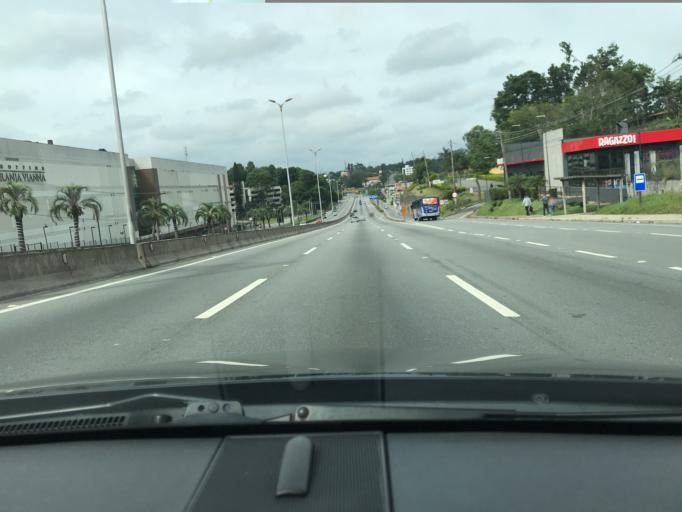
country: BR
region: Sao Paulo
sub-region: Taboao Da Serra
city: Taboao da Serra
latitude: -23.5909
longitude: -46.8324
